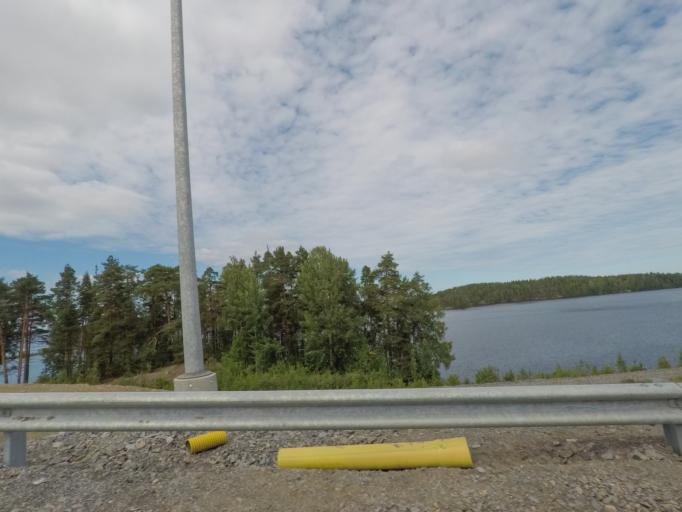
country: FI
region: Southern Savonia
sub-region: Savonlinna
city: Savonlinna
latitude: 61.8794
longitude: 28.8451
